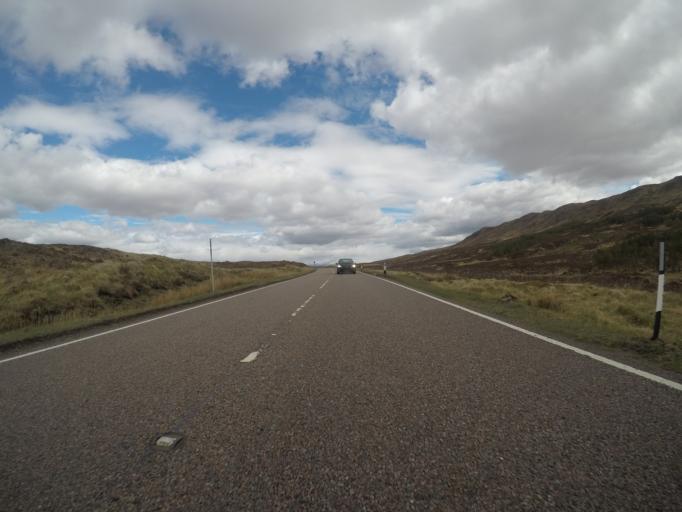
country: GB
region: Scotland
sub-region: Highland
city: Spean Bridge
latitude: 56.5839
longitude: -4.7495
